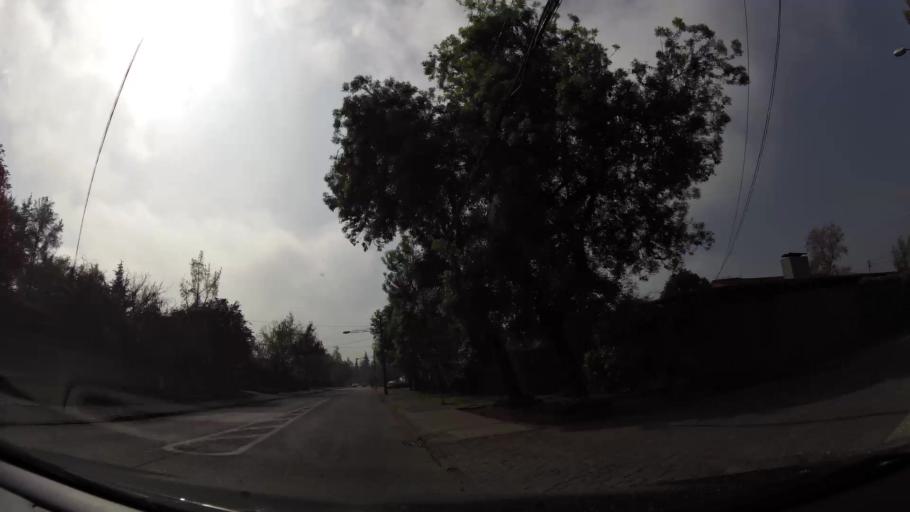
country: CL
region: Santiago Metropolitan
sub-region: Provincia de Santiago
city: Villa Presidente Frei, Nunoa, Santiago, Chile
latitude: -33.3854
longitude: -70.5692
